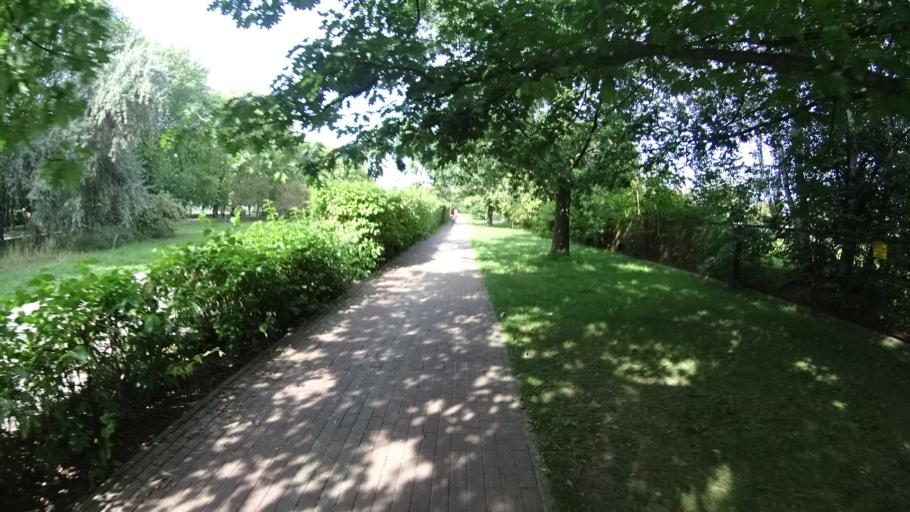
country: PL
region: Masovian Voivodeship
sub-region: Warszawa
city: Ochota
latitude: 52.2365
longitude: 20.9503
